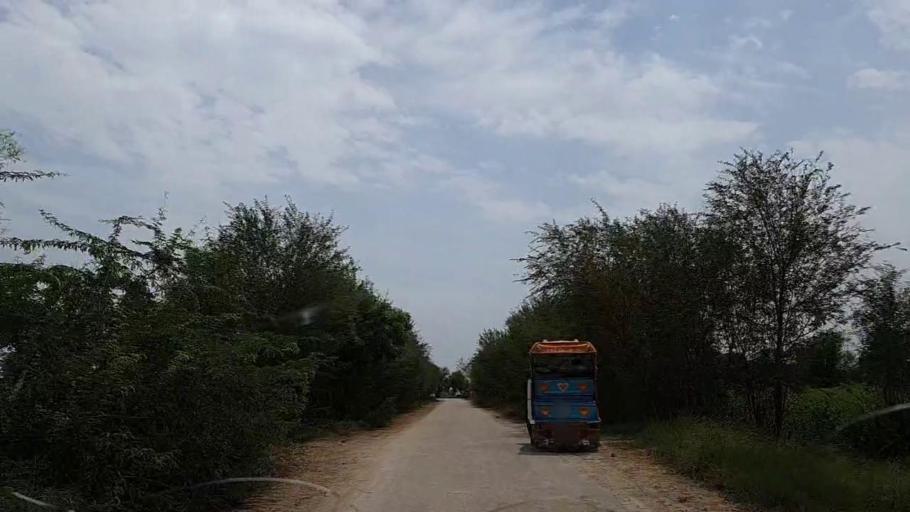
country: PK
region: Sindh
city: Tharu Shah
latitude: 26.9314
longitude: 68.1051
